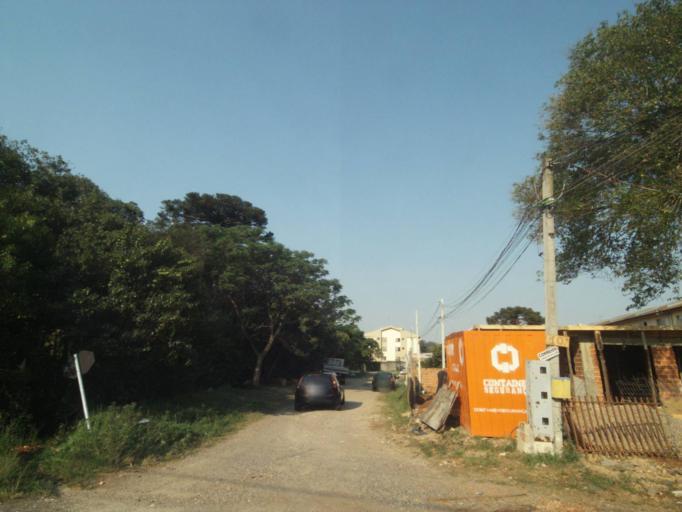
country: BR
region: Parana
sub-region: Curitiba
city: Curitiba
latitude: -25.4918
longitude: -49.2660
